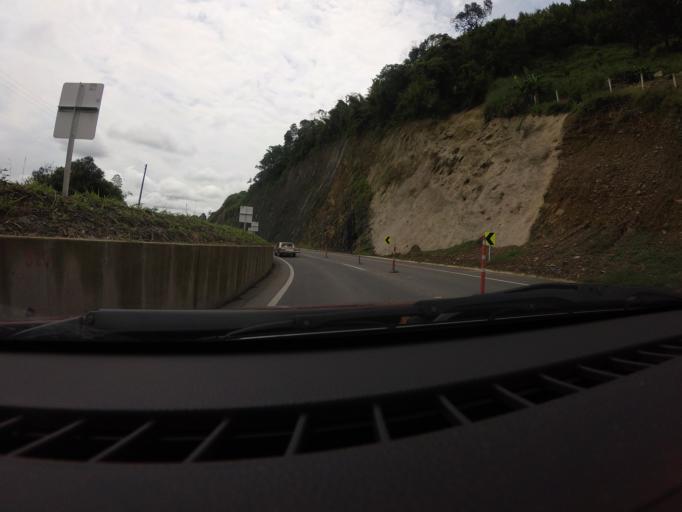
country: CO
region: Cundinamarca
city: La Vega
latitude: 4.9856
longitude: -74.3243
